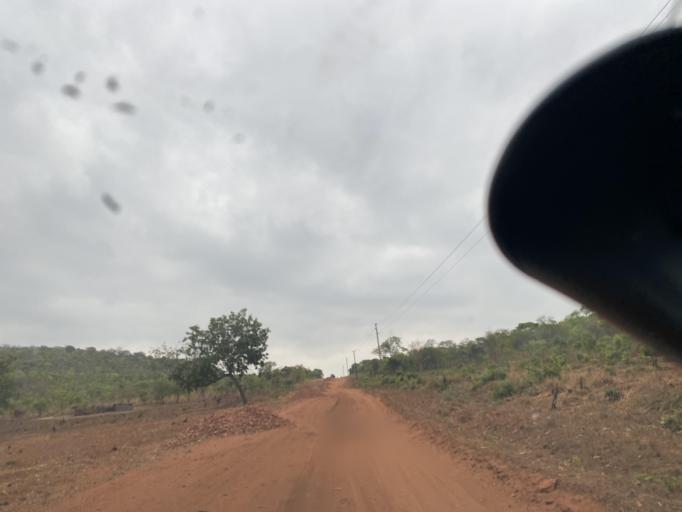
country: ZM
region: Lusaka
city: Chongwe
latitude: -15.1771
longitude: 28.7634
